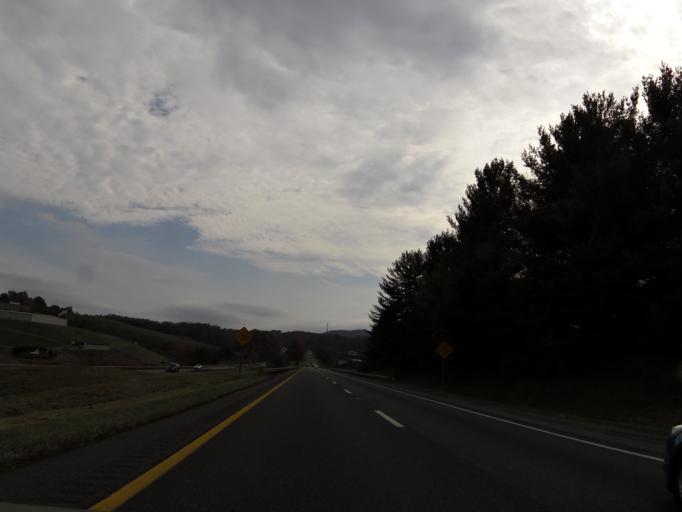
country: US
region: Virginia
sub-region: Carroll County
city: Hillsville
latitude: 36.7478
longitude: -80.7732
